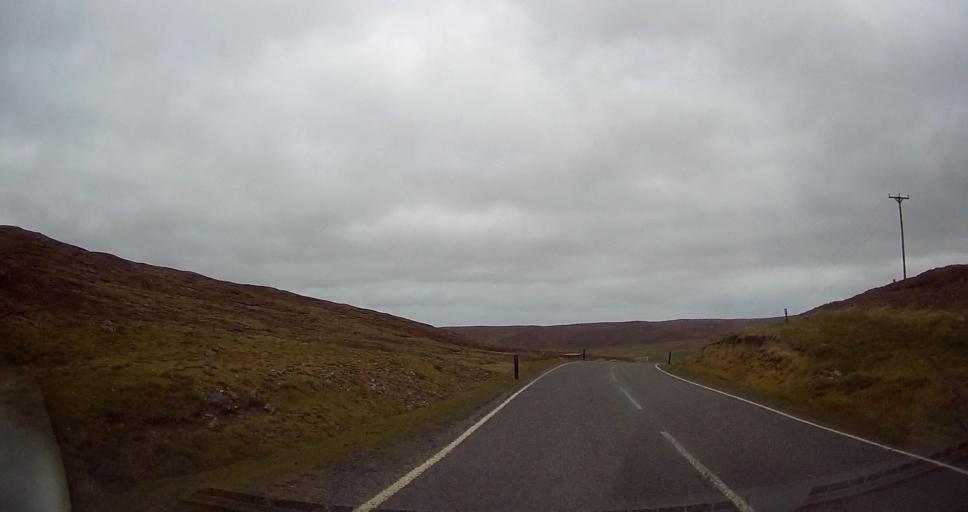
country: GB
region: Scotland
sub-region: Shetland Islands
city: Lerwick
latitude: 60.3431
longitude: -1.2966
